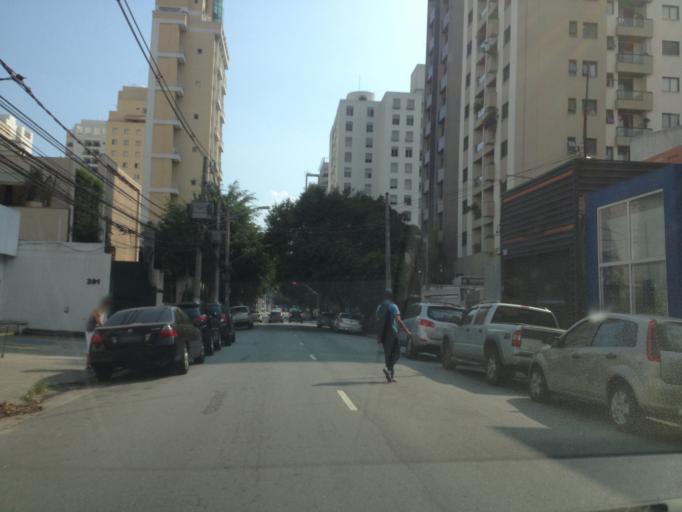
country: BR
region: Sao Paulo
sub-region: Sao Paulo
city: Sao Paulo
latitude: -23.5950
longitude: -46.6756
